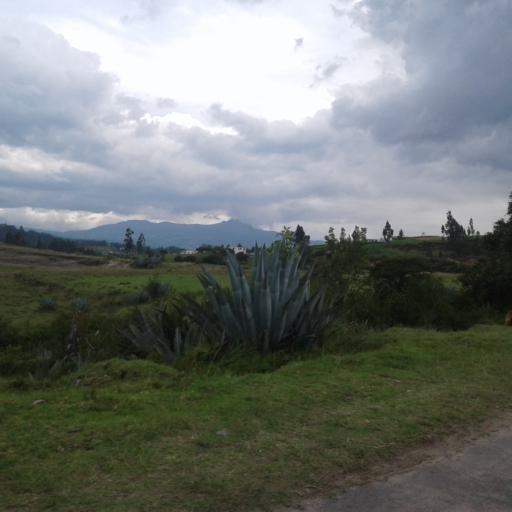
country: EC
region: Pichincha
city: Sangolqui
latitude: -0.2880
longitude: -78.3855
